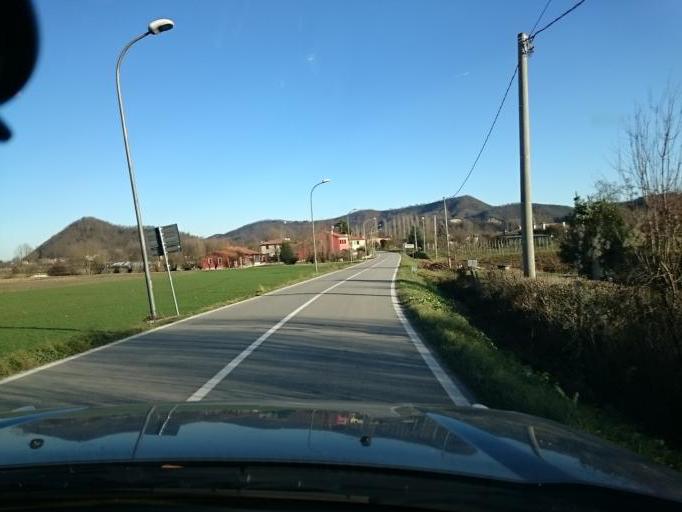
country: IT
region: Veneto
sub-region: Provincia di Padova
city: Treponti
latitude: 45.3666
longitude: 11.6915
